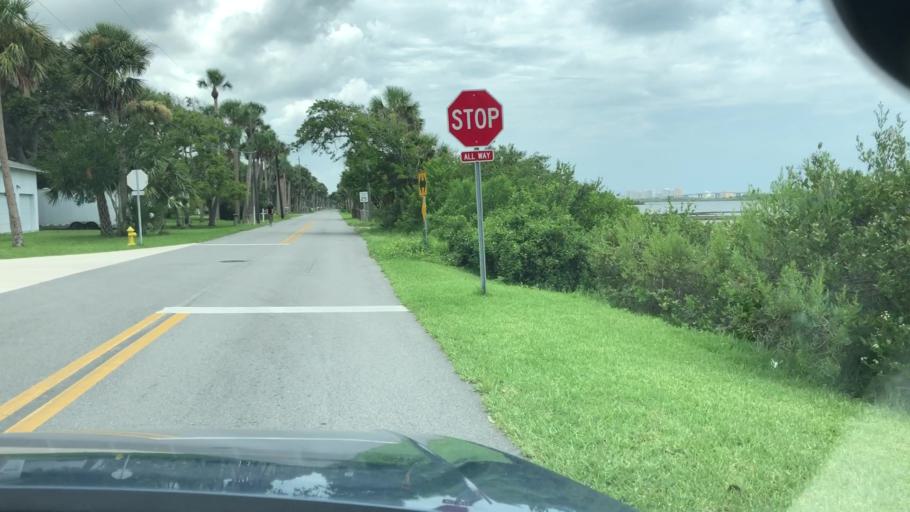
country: US
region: Florida
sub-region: Volusia County
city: Port Orange
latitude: 29.1256
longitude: -80.9766
